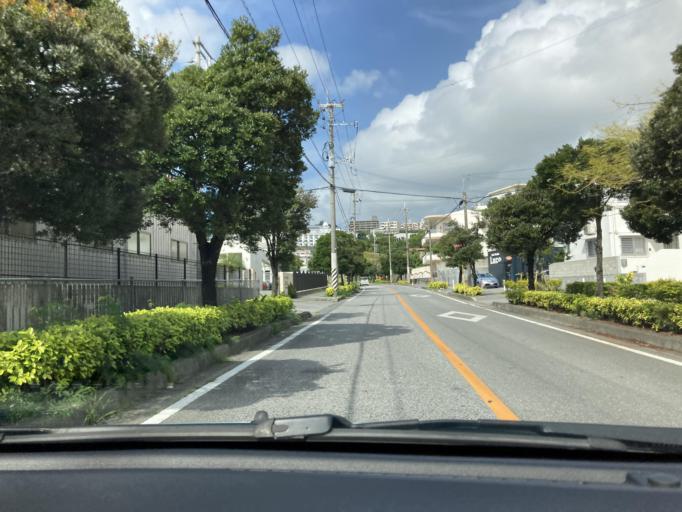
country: JP
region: Okinawa
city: Okinawa
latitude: 26.3207
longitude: 127.8163
